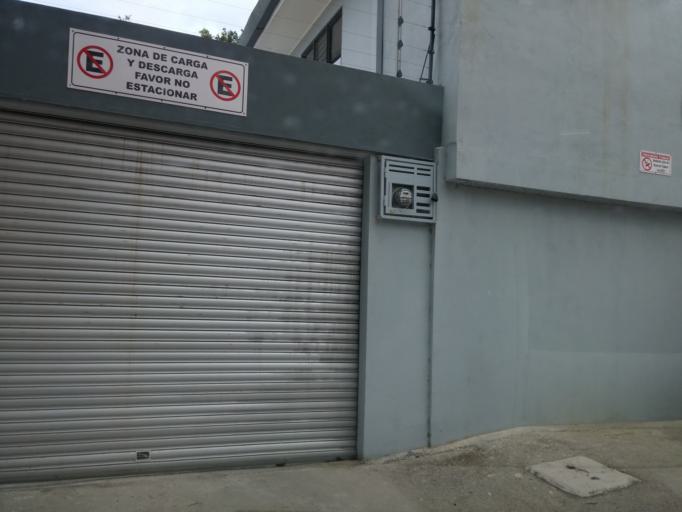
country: CR
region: San Jose
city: San Jose
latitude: 9.9390
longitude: -84.1039
